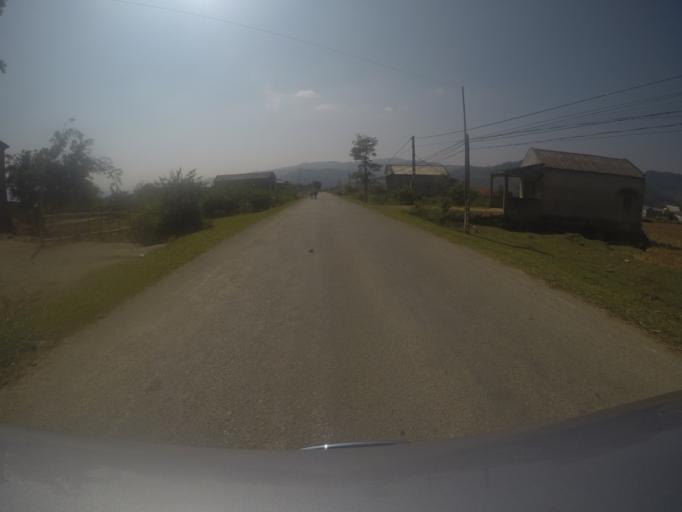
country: VN
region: Lai Chau
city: Than Uyen
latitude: 22.0193
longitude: 103.9248
